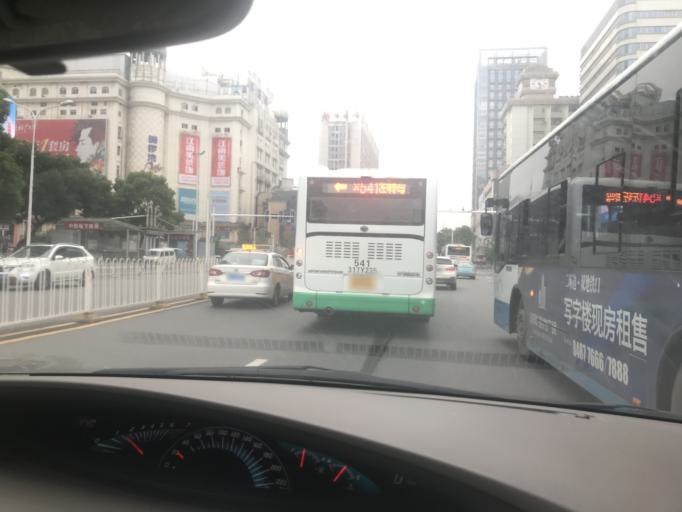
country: CN
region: Hubei
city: Wuhan
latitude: 30.5521
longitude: 114.2594
